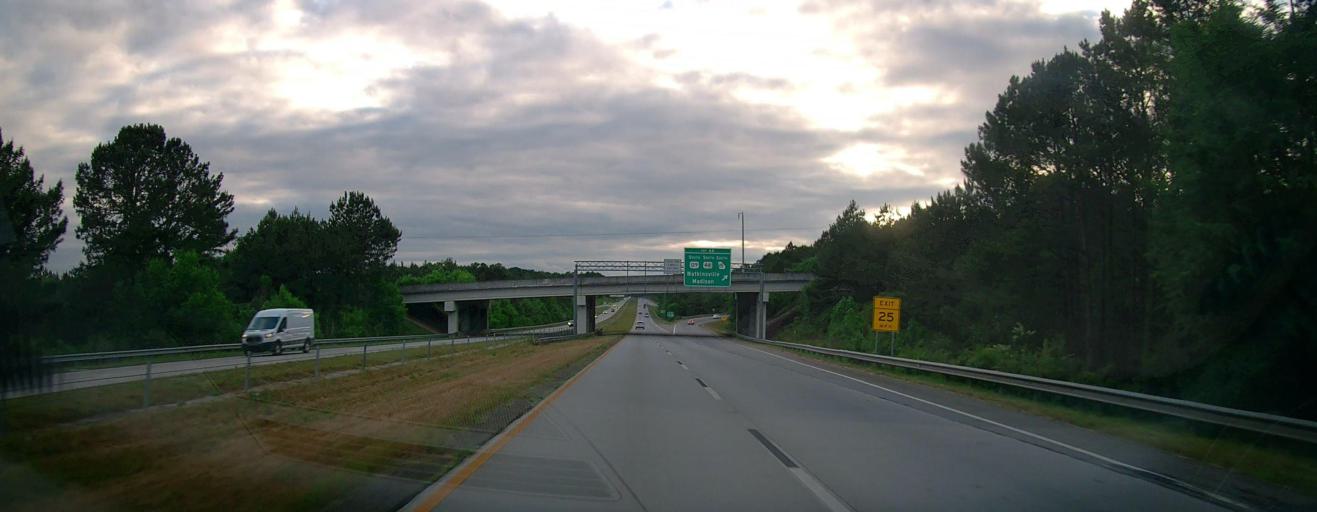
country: US
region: Georgia
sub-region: Clarke County
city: Athens
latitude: 33.9165
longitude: -83.4034
